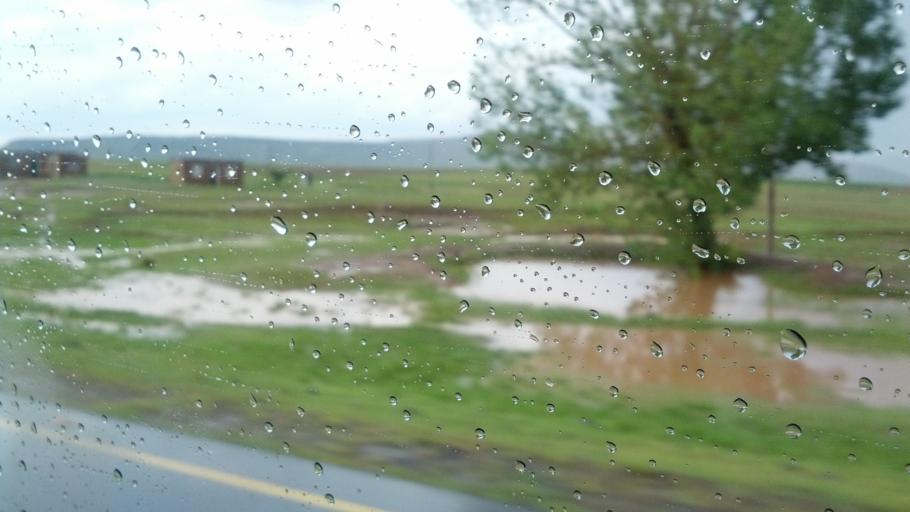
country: LS
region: Mafeteng
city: Mafeteng
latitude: -29.7555
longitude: 27.1285
